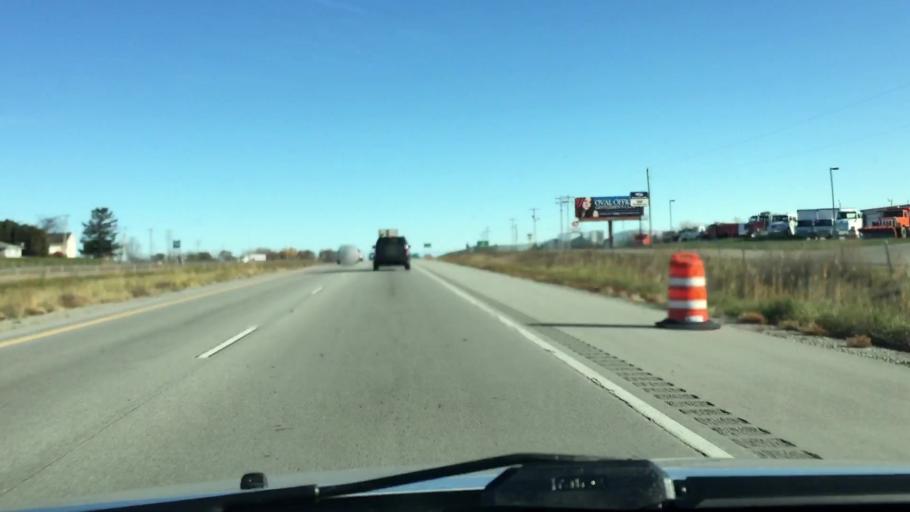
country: US
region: Wisconsin
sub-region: Brown County
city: De Pere
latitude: 44.4145
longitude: -88.1347
